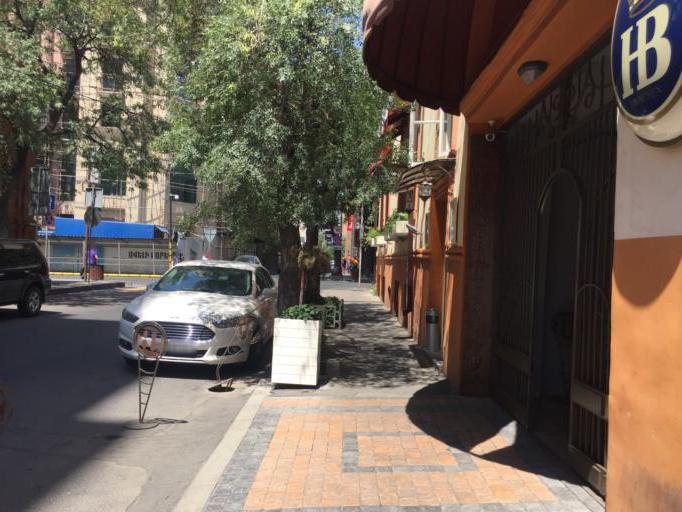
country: AM
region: Yerevan
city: Yerevan
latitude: 40.1805
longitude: 44.5157
